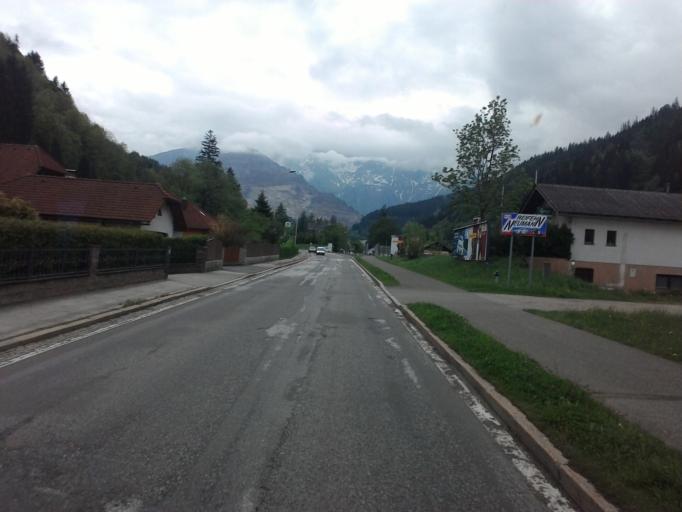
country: AT
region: Styria
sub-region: Politischer Bezirk Leoben
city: Eisenerz
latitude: 47.5536
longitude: 14.8726
